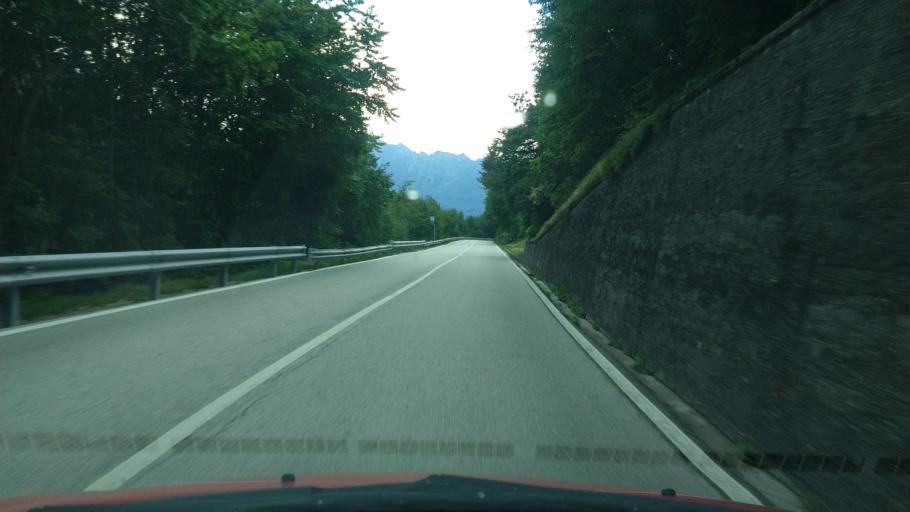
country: IT
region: Veneto
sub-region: Provincia di Vicenza
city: Arsiero
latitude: 45.8258
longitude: 11.3634
